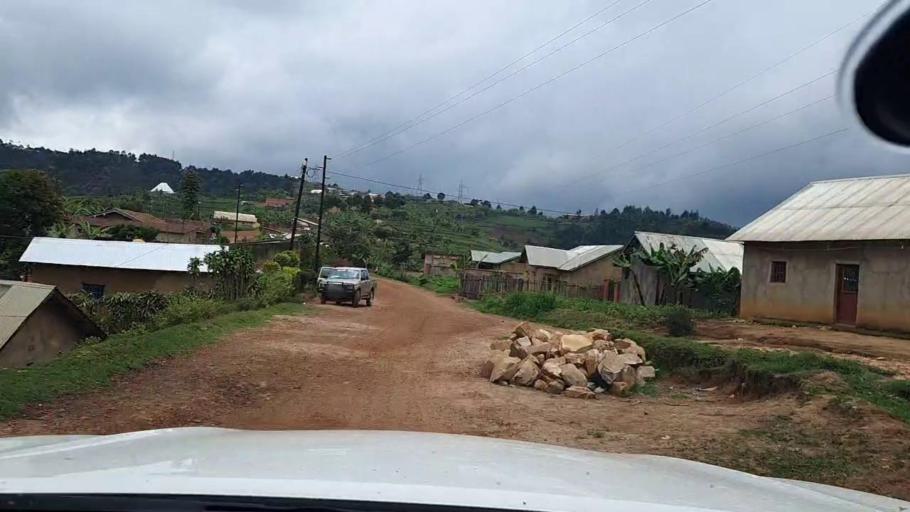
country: RW
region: Western Province
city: Kibuye
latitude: -2.1740
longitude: 29.4391
